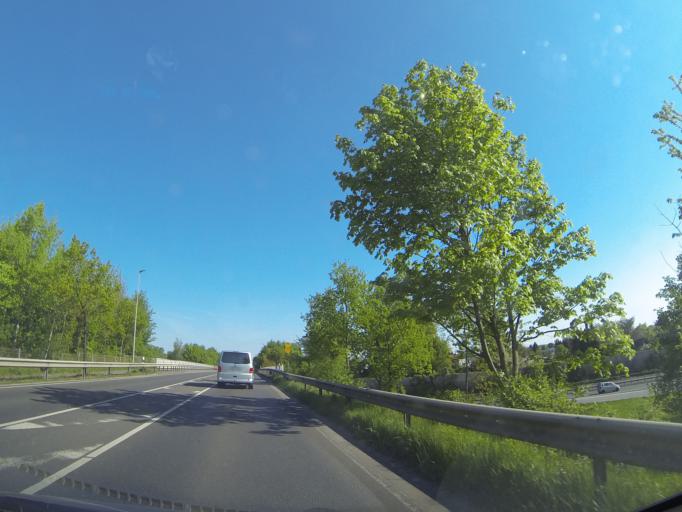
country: DE
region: Schleswig-Holstein
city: Halstenbek
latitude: 53.6390
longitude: 9.8386
